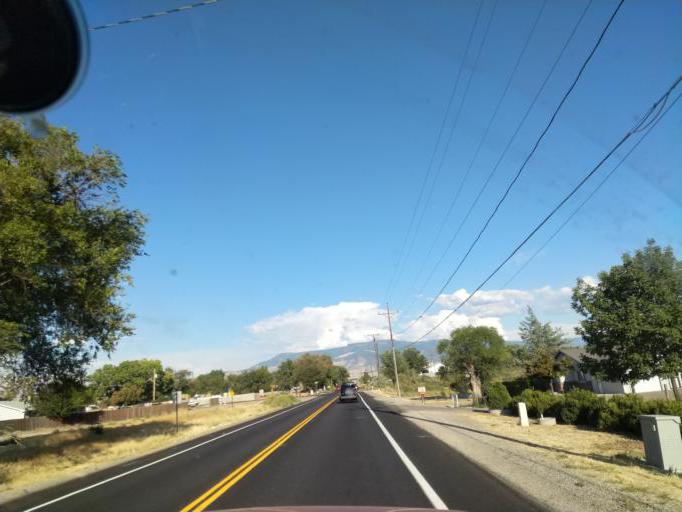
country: US
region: Colorado
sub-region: Mesa County
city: Fruitvale
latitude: 39.0628
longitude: -108.4795
